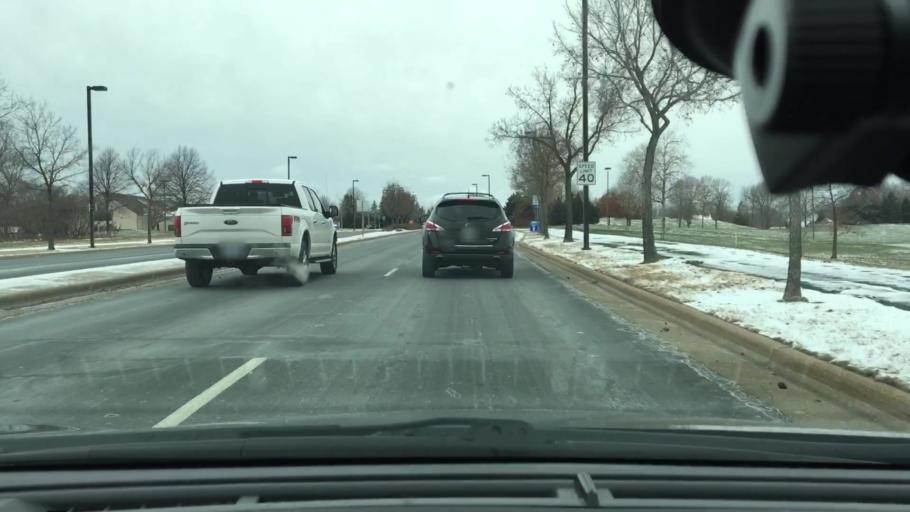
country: US
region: Minnesota
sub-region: Hennepin County
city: Maple Grove
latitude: 45.1028
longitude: -93.4687
